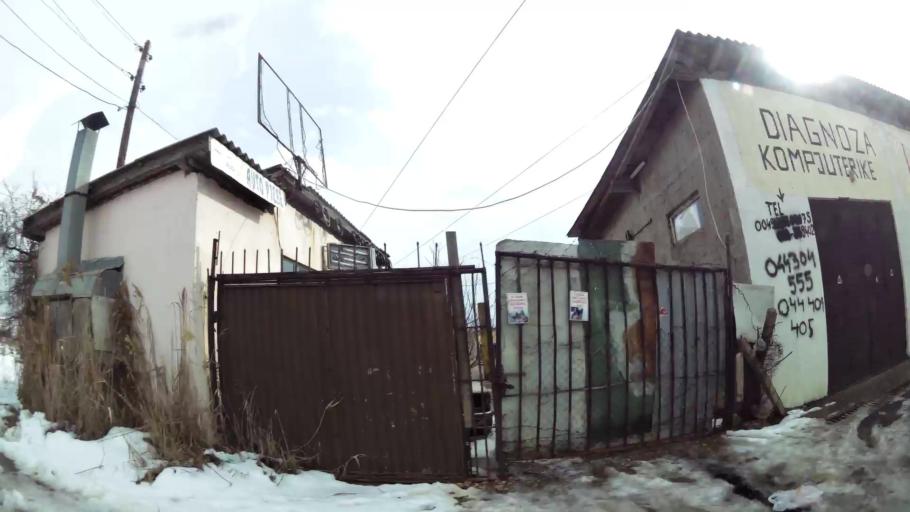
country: XK
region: Pristina
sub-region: Komuna e Prishtines
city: Pristina
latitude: 42.6930
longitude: 21.1669
